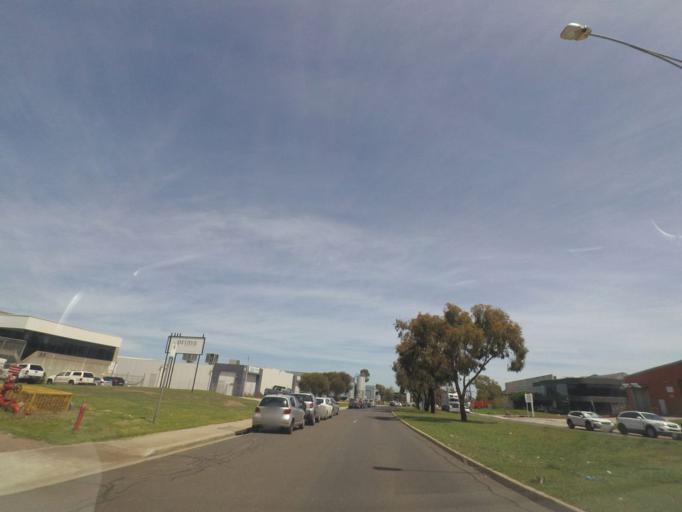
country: AU
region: Victoria
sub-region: Hume
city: Tullamarine
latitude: -37.7106
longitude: 144.8707
